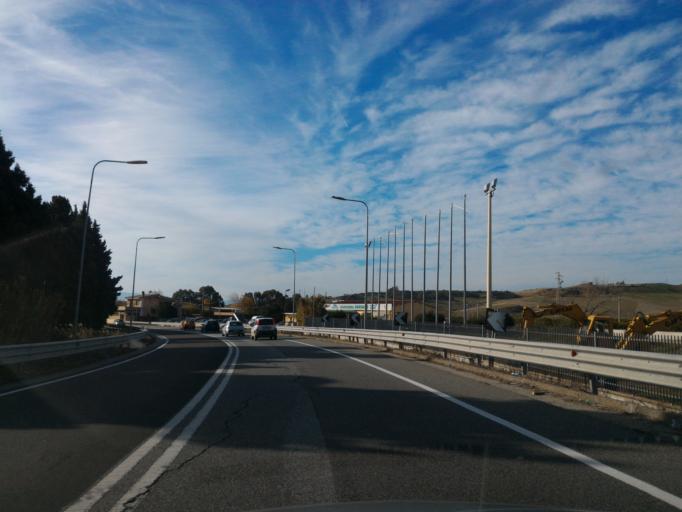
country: IT
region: Calabria
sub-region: Provincia di Catanzaro
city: Sellia Marina
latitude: 38.8844
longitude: 16.7110
